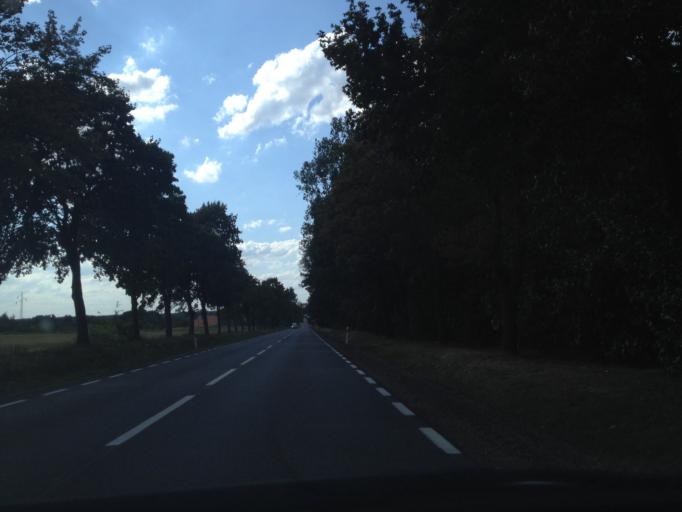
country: PL
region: Lubusz
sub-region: Powiat zarski
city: Lipinki Luzyckie
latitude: 51.6367
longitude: 15.0143
